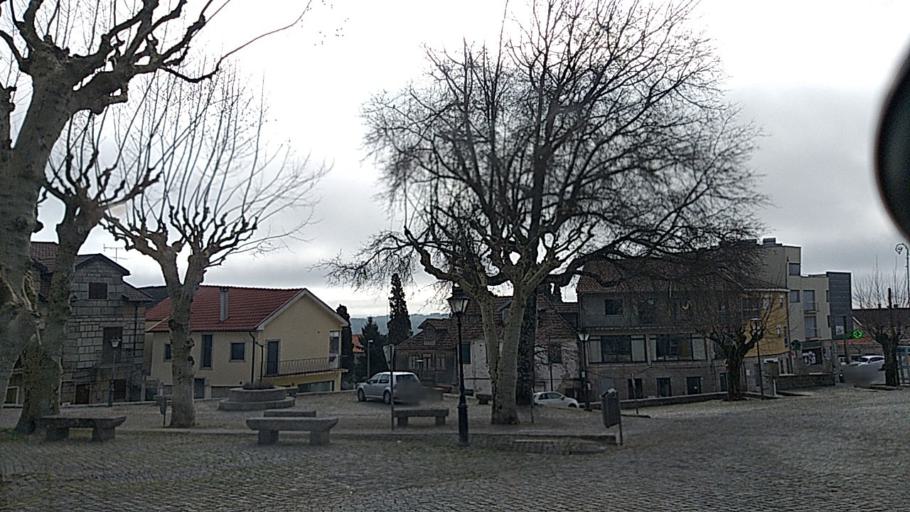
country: PT
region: Guarda
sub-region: Aguiar da Beira
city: Aguiar da Beira
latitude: 40.8178
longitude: -7.5440
